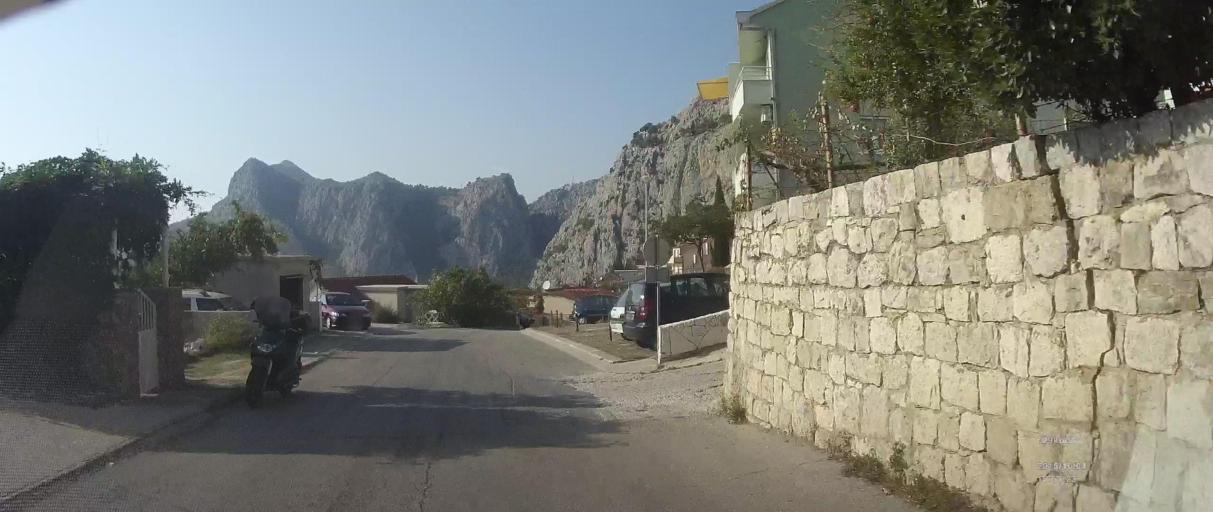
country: HR
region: Splitsko-Dalmatinska
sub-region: Grad Omis
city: Omis
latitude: 43.4397
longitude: 16.7007
